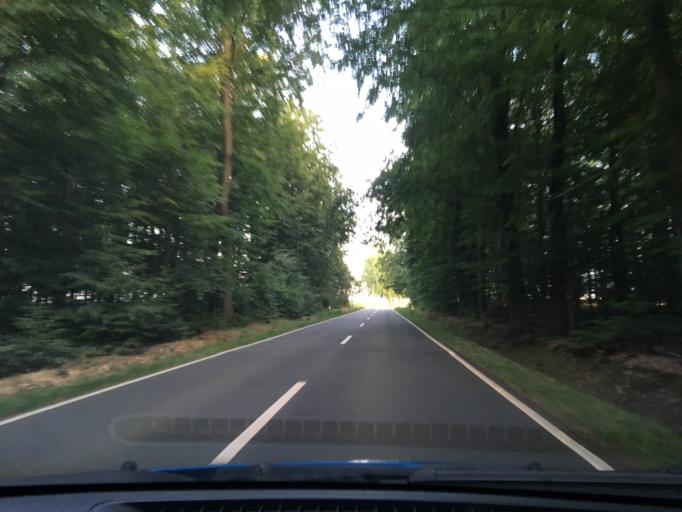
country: DE
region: Lower Saxony
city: Tosterglope
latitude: 53.2238
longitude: 10.8083
